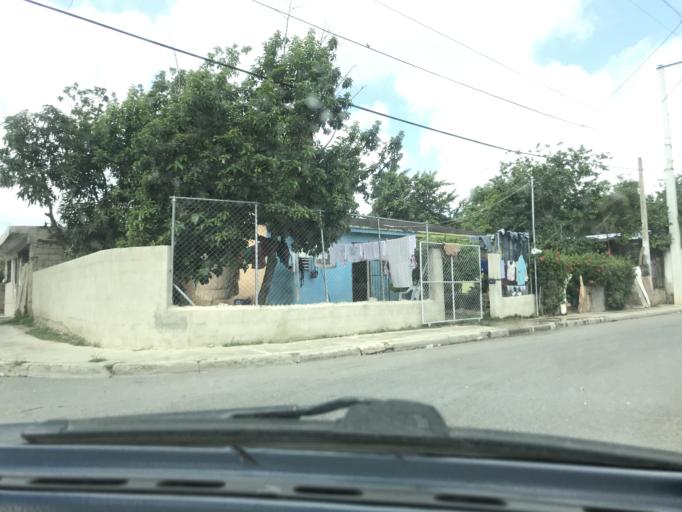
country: DO
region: Santiago
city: Santiago de los Caballeros
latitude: 19.4508
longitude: -70.7300
